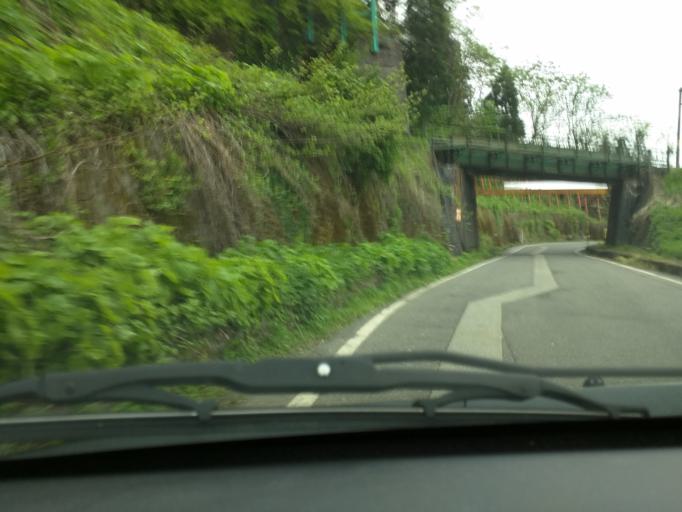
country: JP
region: Niigata
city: Muikamachi
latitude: 37.2081
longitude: 138.9511
